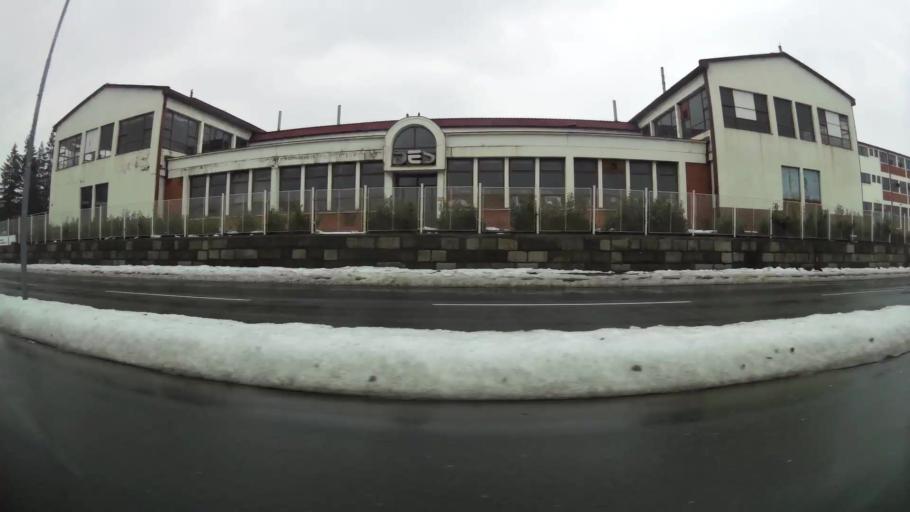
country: RS
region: Central Serbia
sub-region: Belgrade
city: Vozdovac
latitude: 44.7665
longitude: 20.4860
